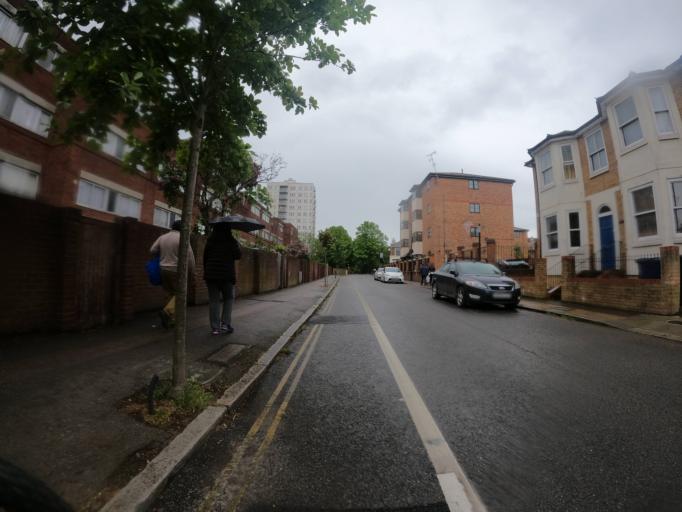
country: GB
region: England
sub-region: Greater London
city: Acton
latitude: 51.5060
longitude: -0.2743
